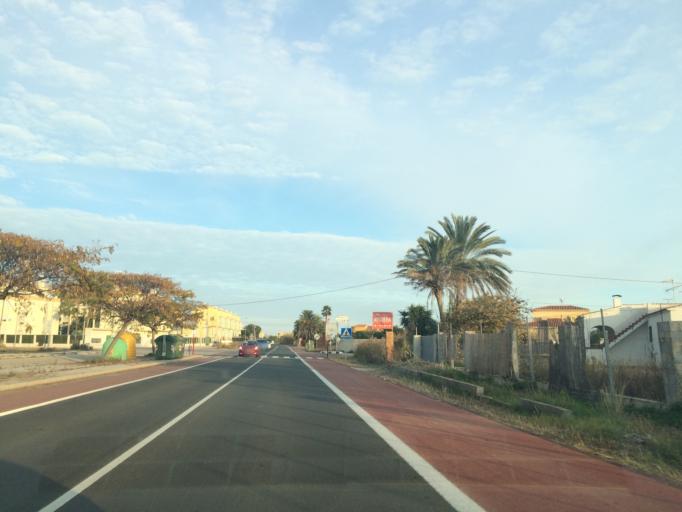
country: ES
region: Valencia
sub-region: Provincia de Alicante
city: els Poblets
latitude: 38.8581
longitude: 0.0378
